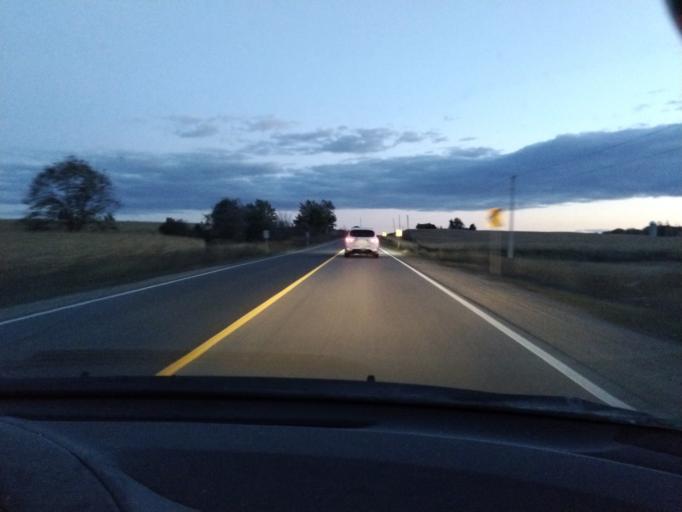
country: CA
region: Ontario
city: Bradford West Gwillimbury
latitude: 44.1045
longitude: -79.6408
